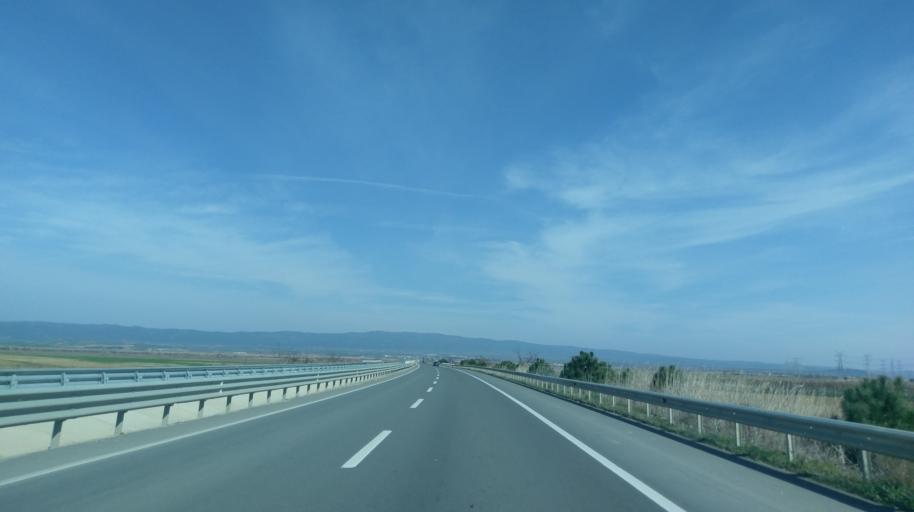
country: TR
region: Canakkale
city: Evrese
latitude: 40.6067
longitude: 26.8644
